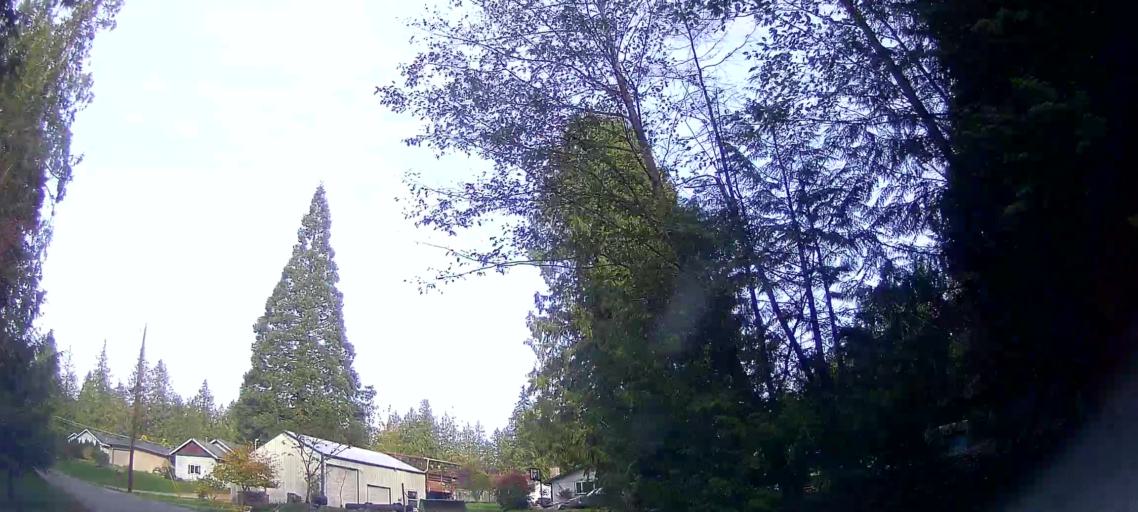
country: US
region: Washington
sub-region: Snohomish County
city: Stanwood
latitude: 48.2796
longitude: -122.3400
